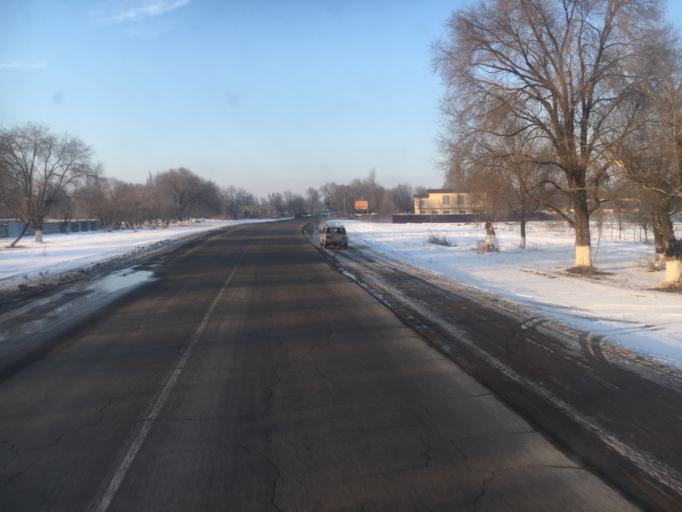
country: KZ
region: Almaty Oblysy
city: Burunday
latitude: 43.3642
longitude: 76.6422
